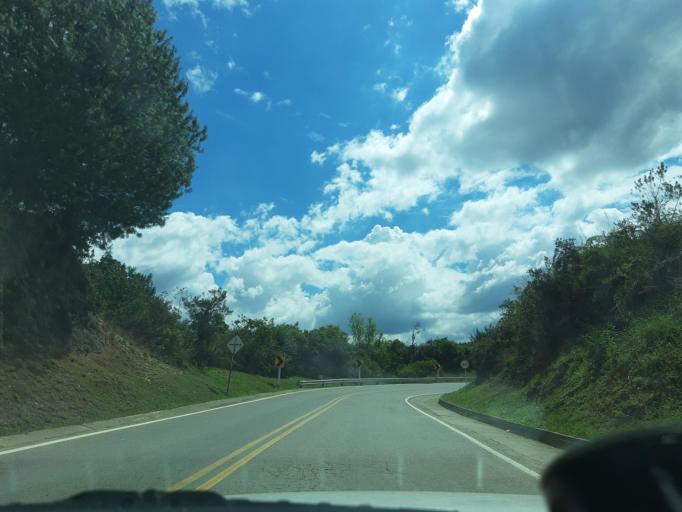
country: CO
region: Boyaca
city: Raquira
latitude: 5.5666
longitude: -73.6683
